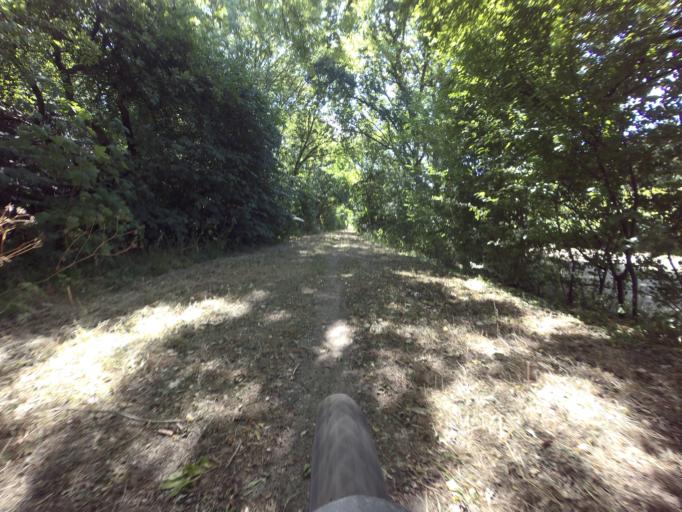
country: DK
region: Central Jutland
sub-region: Odder Kommune
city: Odder
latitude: 55.9225
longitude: 10.1089
